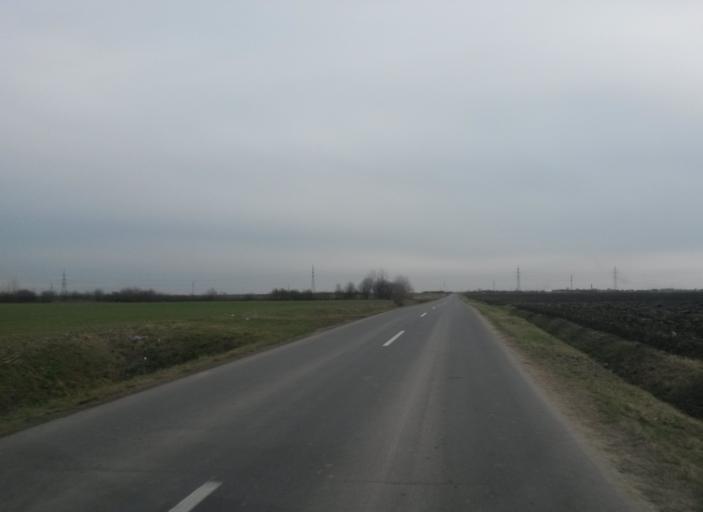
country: HR
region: Osjecko-Baranjska
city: Ovcara
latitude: 45.4994
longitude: 18.6087
